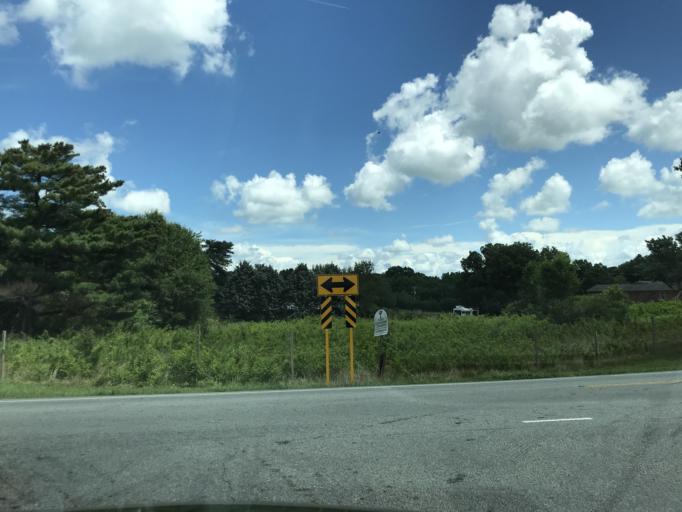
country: US
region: North Carolina
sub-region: Lincoln County
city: Lincolnton
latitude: 35.5023
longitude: -81.2085
